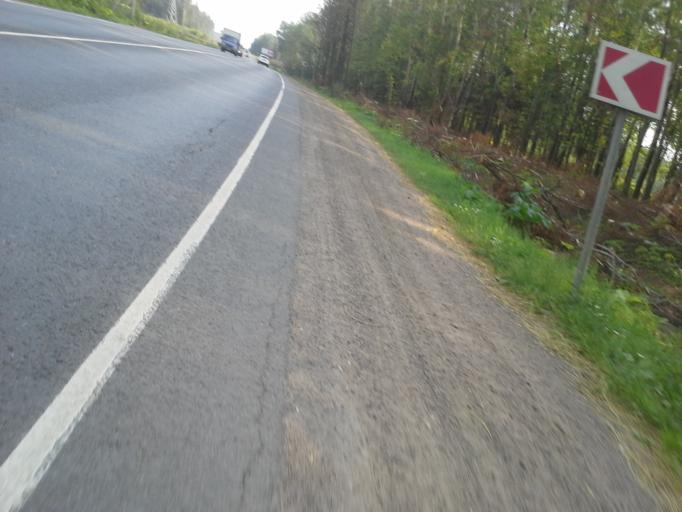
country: RU
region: Moskovskaya
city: Istra
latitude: 55.9227
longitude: 36.9462
